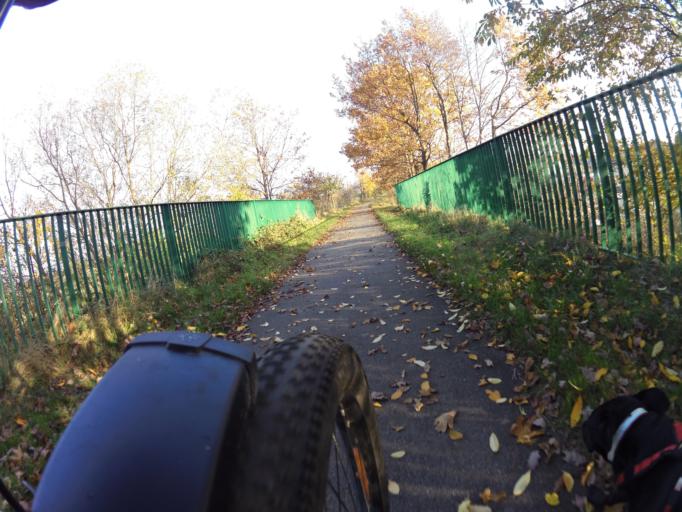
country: PL
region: Pomeranian Voivodeship
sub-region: Powiat pucki
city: Krokowa
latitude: 54.7825
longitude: 18.1680
